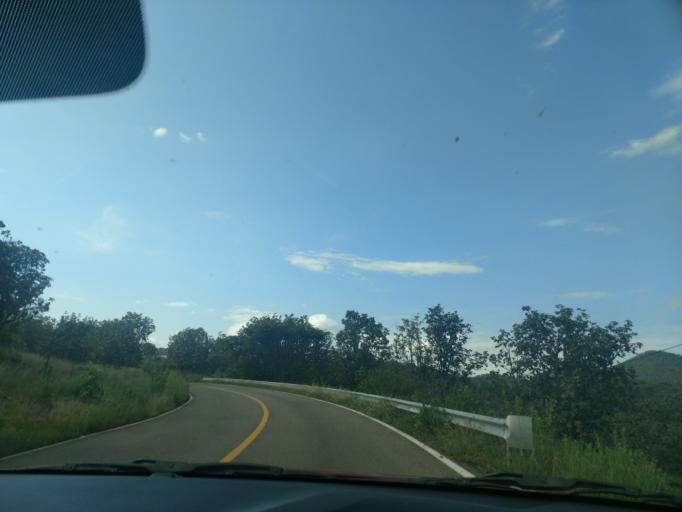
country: MX
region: Jalisco
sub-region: Atengo
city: Soyatlan del Oro
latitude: 20.5015
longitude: -104.3547
